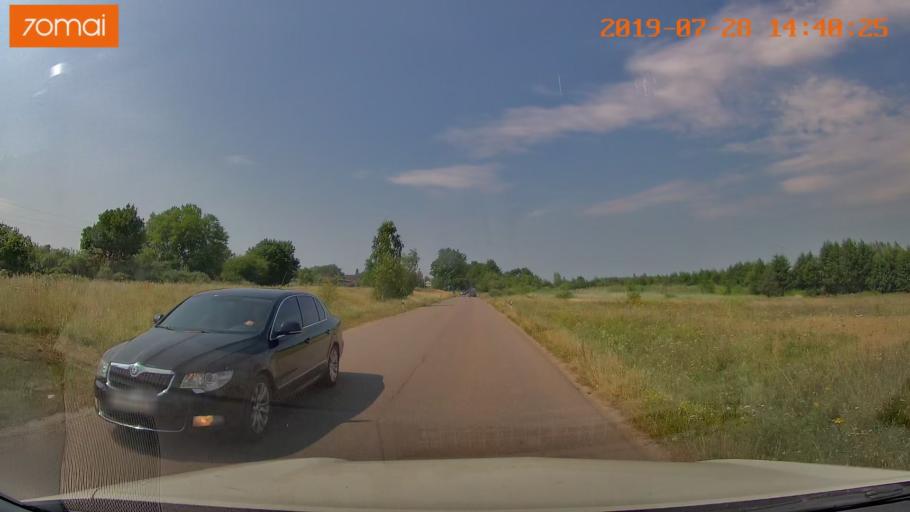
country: RU
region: Kaliningrad
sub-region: Gorod Kaliningrad
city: Yantarnyy
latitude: 54.8514
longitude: 19.9581
